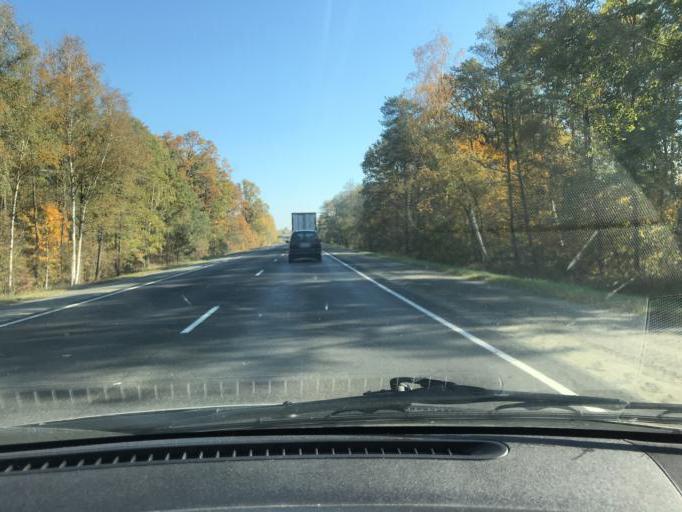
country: BY
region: Brest
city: Mikashevichy
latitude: 52.2443
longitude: 27.4340
